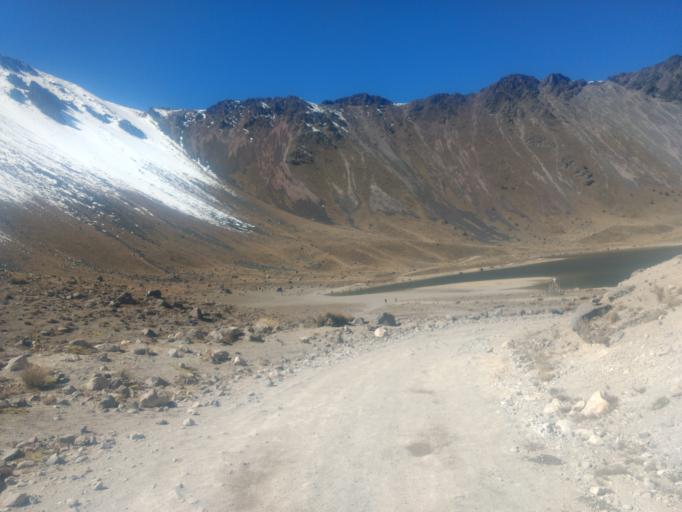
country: MX
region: Mexico
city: Cerro La Calera
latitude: 19.1061
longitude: -99.7566
